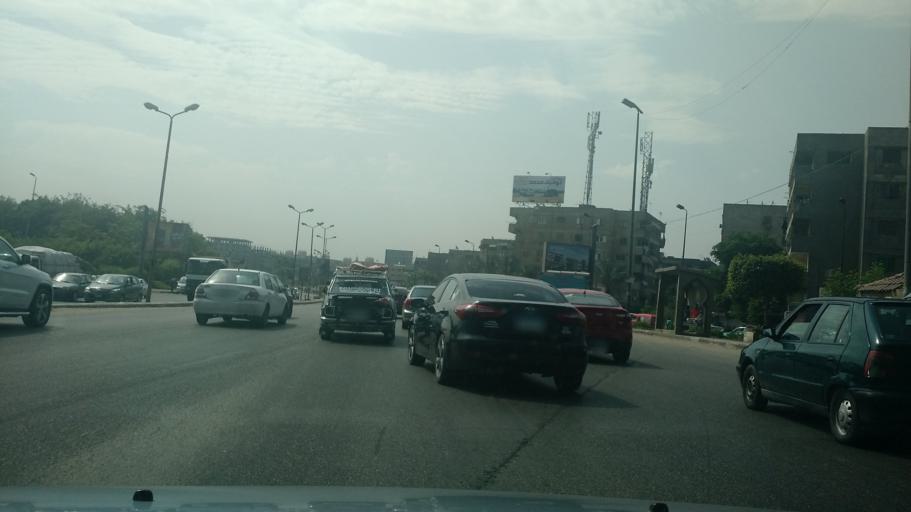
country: EG
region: Al Jizah
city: Al Jizah
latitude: 29.9913
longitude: 31.2836
